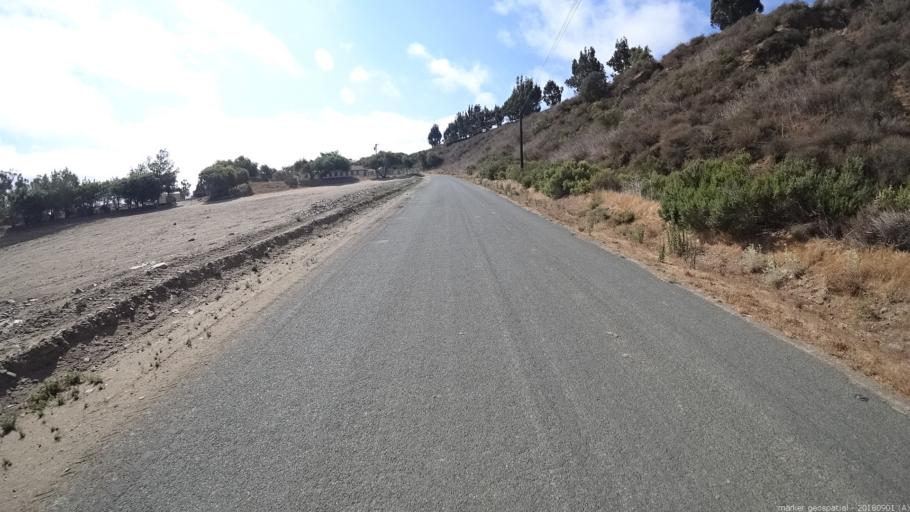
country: US
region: California
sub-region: Monterey County
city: Soledad
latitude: 36.3953
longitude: -121.3701
